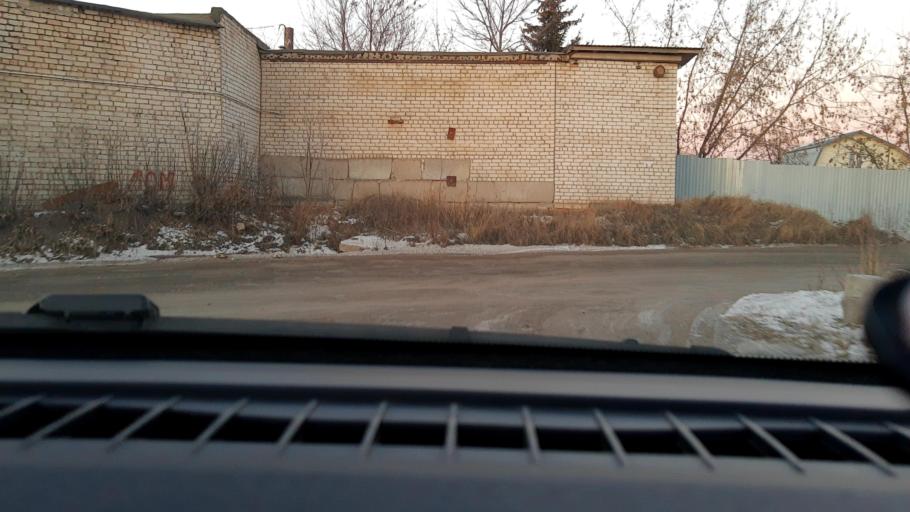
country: RU
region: Nizjnij Novgorod
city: Gorbatovka
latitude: 56.2545
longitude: 43.8347
